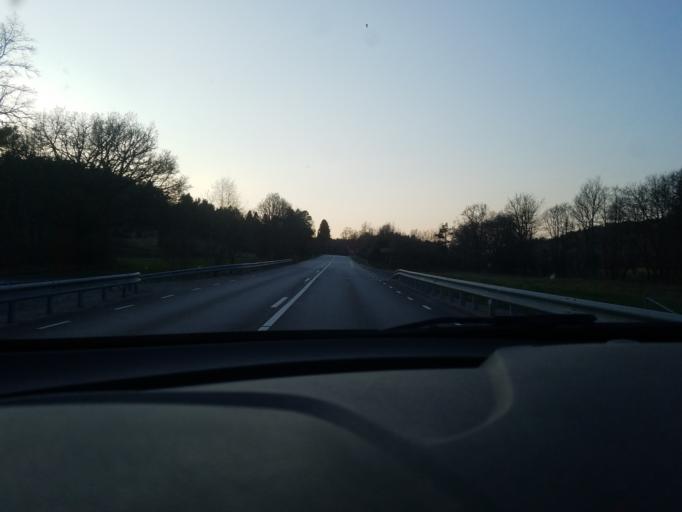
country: SE
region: Vaestra Goetaland
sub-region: Tjorns Kommun
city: Myggenas
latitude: 58.1347
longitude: 11.7165
